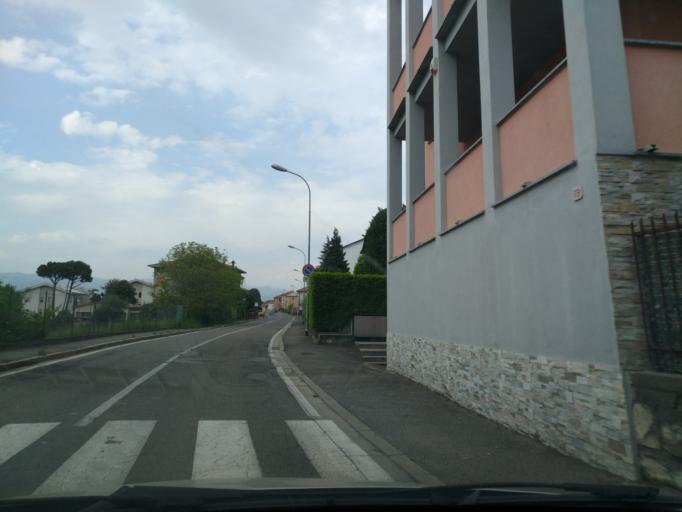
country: IT
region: Lombardy
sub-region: Provincia di Como
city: Cantu
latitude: 45.7236
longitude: 9.1499
